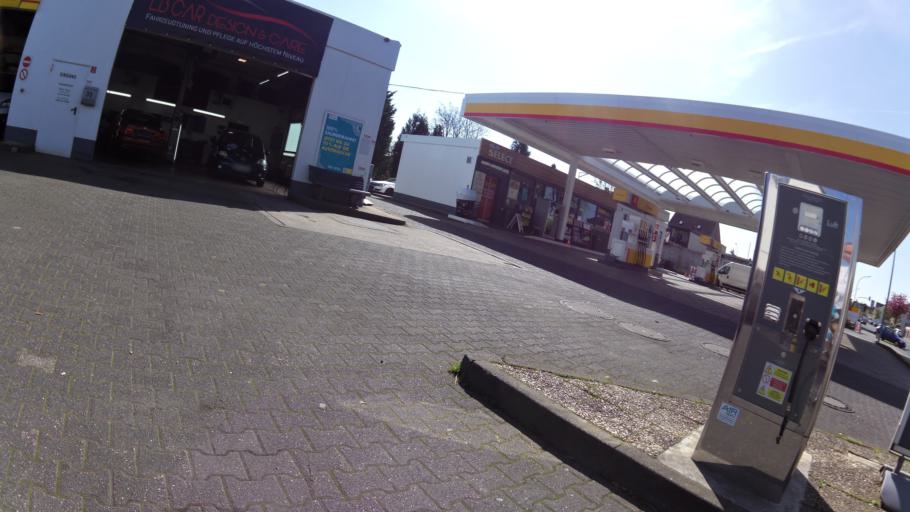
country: DE
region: North Rhine-Westphalia
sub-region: Regierungsbezirk Koln
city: Ubach-Palenberg
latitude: 50.9130
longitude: 6.1373
